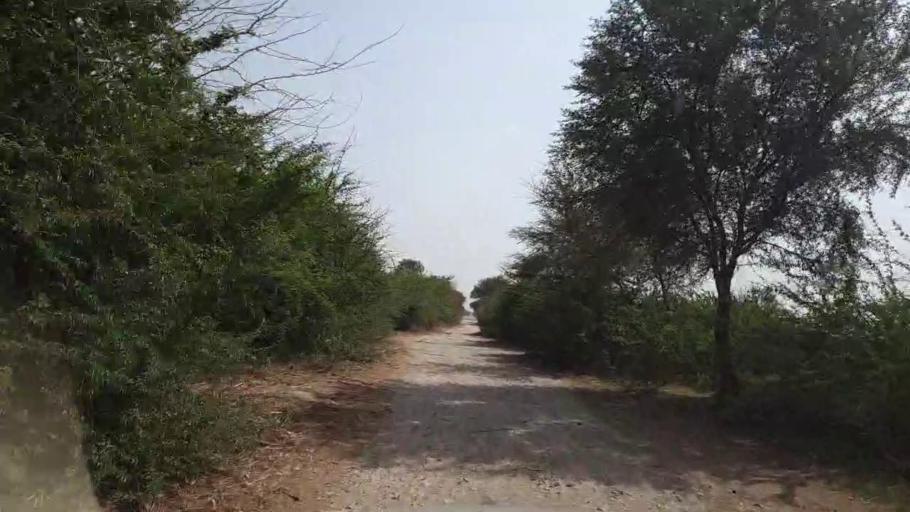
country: PK
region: Sindh
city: Rajo Khanani
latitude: 25.0317
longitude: 68.8731
